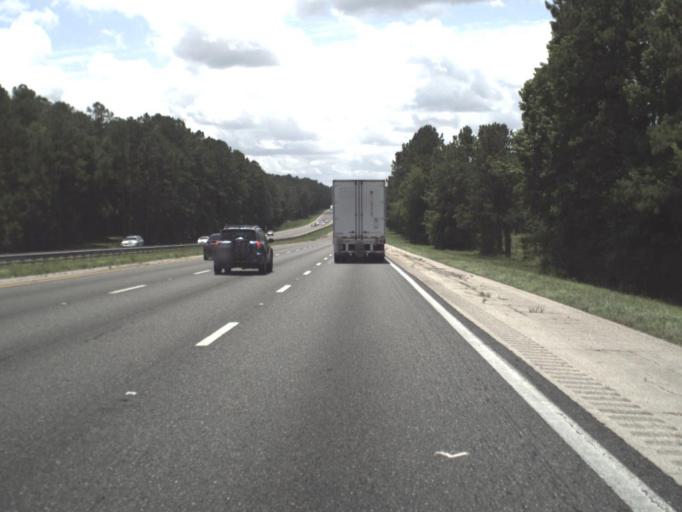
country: US
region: Florida
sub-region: Alachua County
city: Alachua
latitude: 29.7302
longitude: -82.4736
